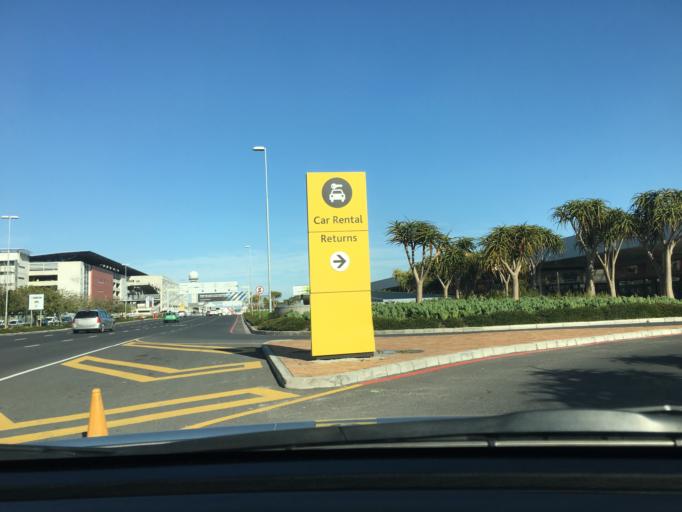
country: ZA
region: Western Cape
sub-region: City of Cape Town
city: Lansdowne
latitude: -33.9688
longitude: 18.5951
